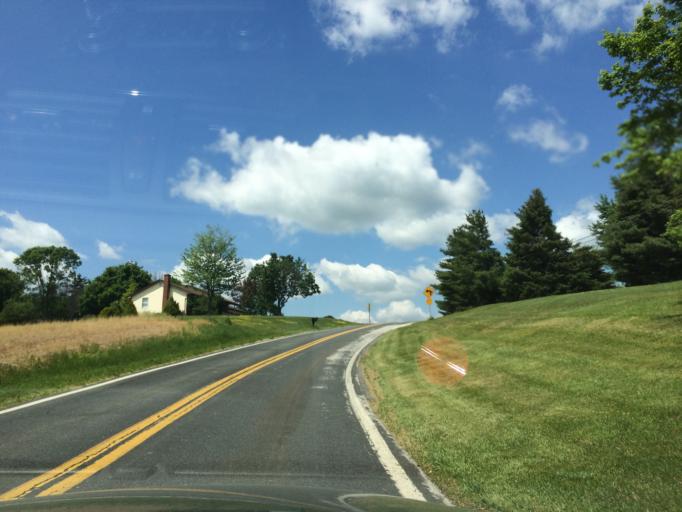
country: US
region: Maryland
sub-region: Carroll County
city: New Windsor
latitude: 39.4568
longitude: -77.0518
